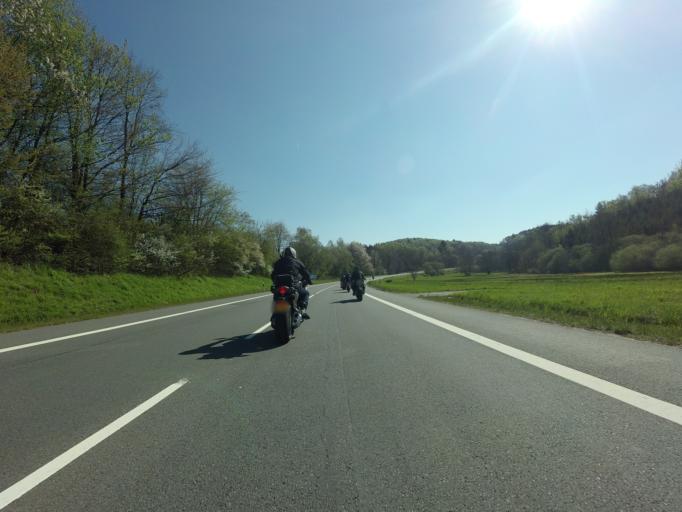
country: DE
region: North Rhine-Westphalia
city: Meinerzhagen
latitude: 51.1086
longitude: 7.7173
